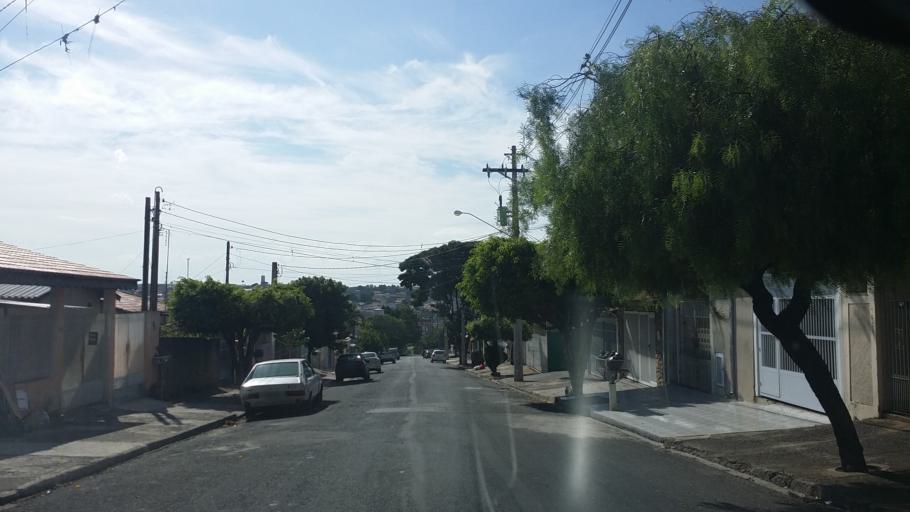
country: BR
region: Sao Paulo
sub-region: Indaiatuba
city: Indaiatuba
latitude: -23.1222
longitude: -47.2390
